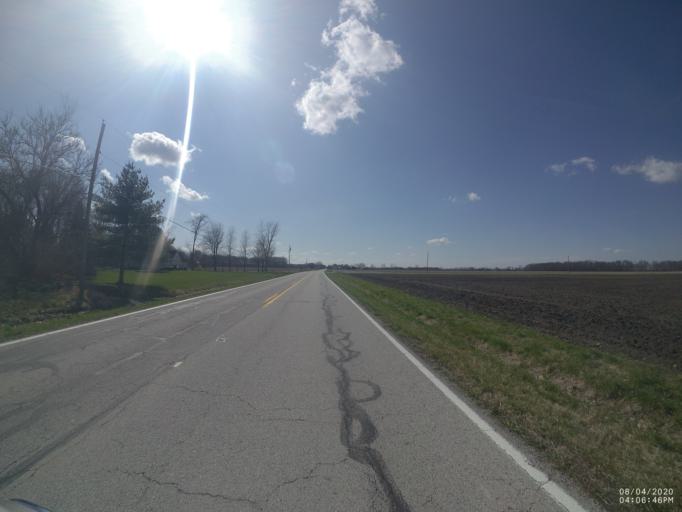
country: US
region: Ohio
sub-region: Sandusky County
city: Ballville
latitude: 41.2683
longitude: -83.2145
